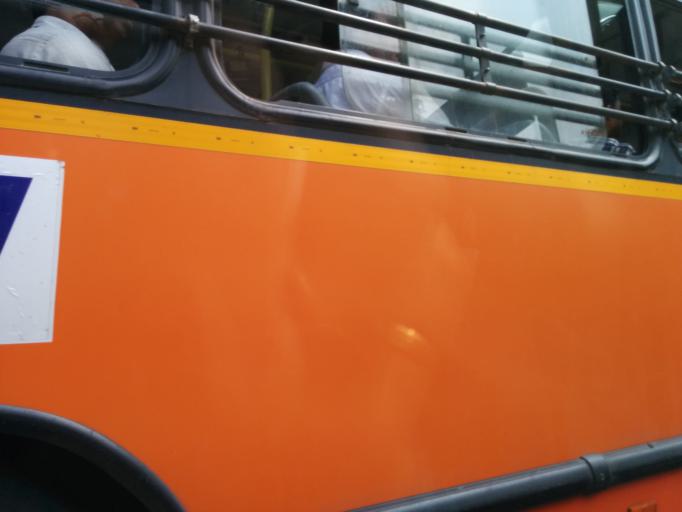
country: IN
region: NCT
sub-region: New Delhi
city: New Delhi
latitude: 28.5432
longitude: 77.2138
